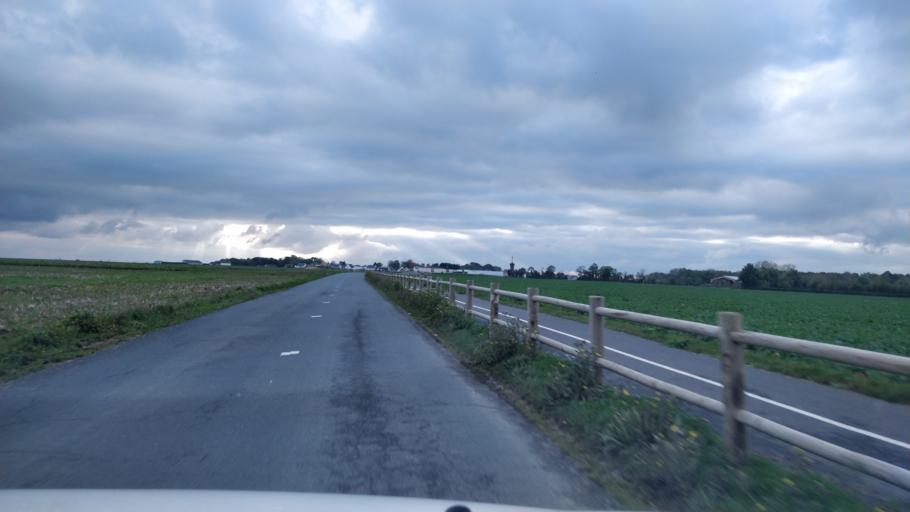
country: FR
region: Lower Normandy
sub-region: Departement du Calvados
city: Ouistreham
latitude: 49.2662
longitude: -0.2716
